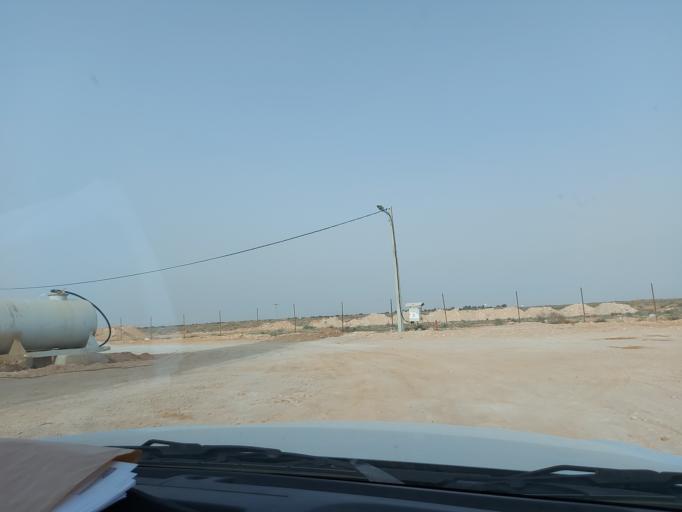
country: TN
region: Madanin
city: Medenine
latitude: 33.2682
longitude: 10.5717
